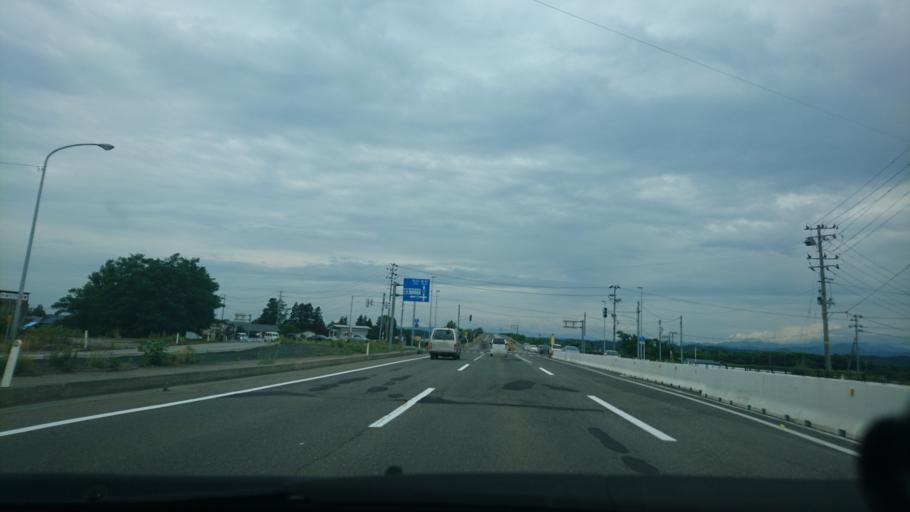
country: JP
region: Akita
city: Omagari
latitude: 39.4871
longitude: 140.4533
